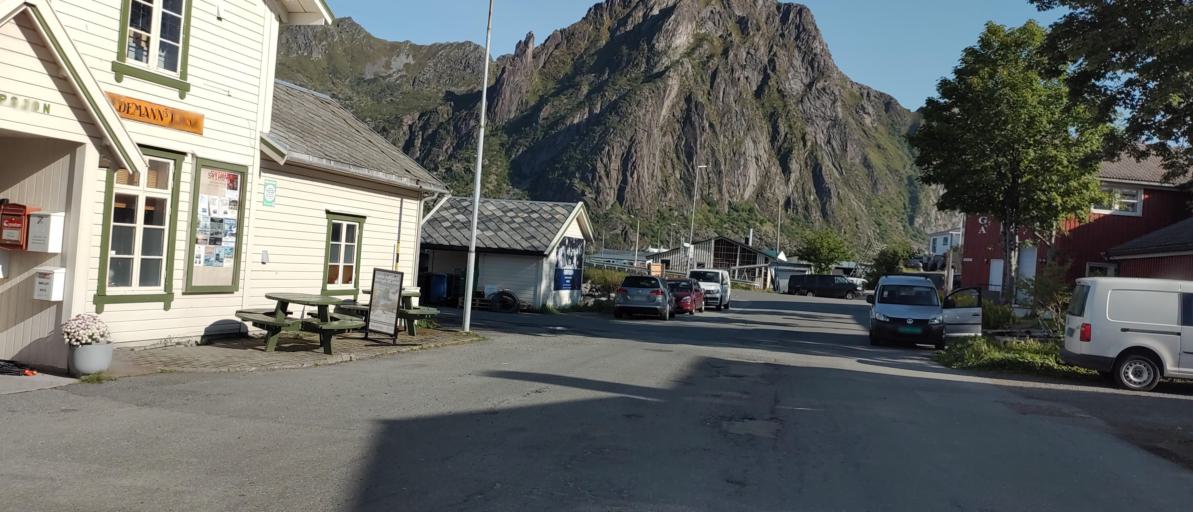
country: NO
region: Nordland
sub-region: Vagan
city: Svolvaer
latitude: 68.2343
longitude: 14.5797
